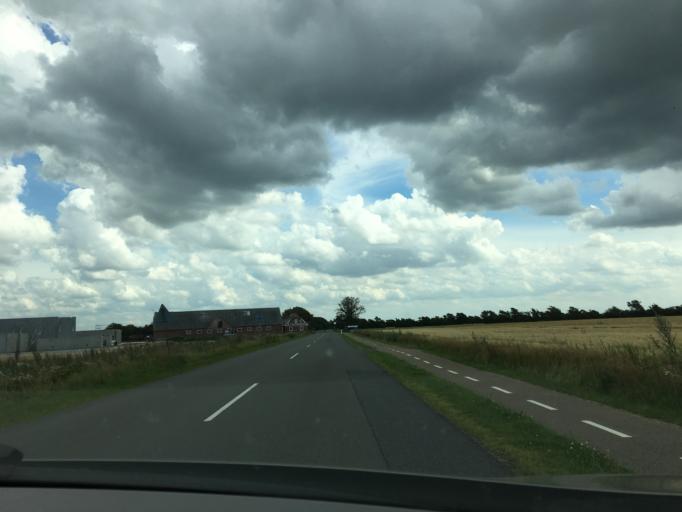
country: DK
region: Central Jutland
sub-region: Ringkobing-Skjern Kommune
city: Skjern
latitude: 55.9534
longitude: 8.4006
